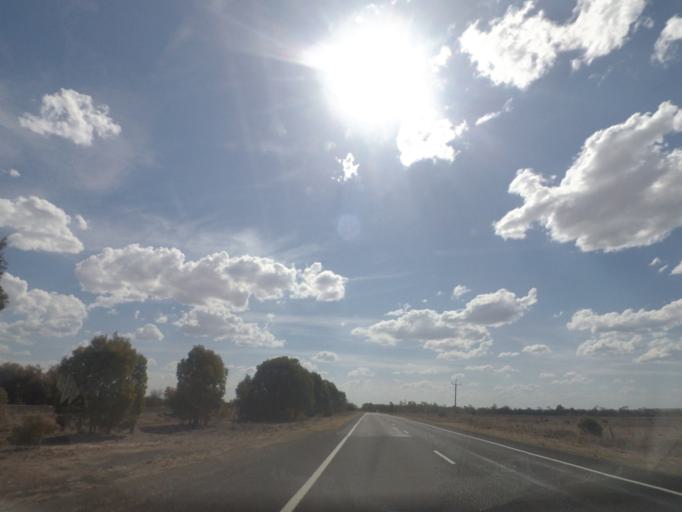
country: AU
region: New South Wales
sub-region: Moree Plains
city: Boggabilla
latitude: -28.4149
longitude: 151.1274
